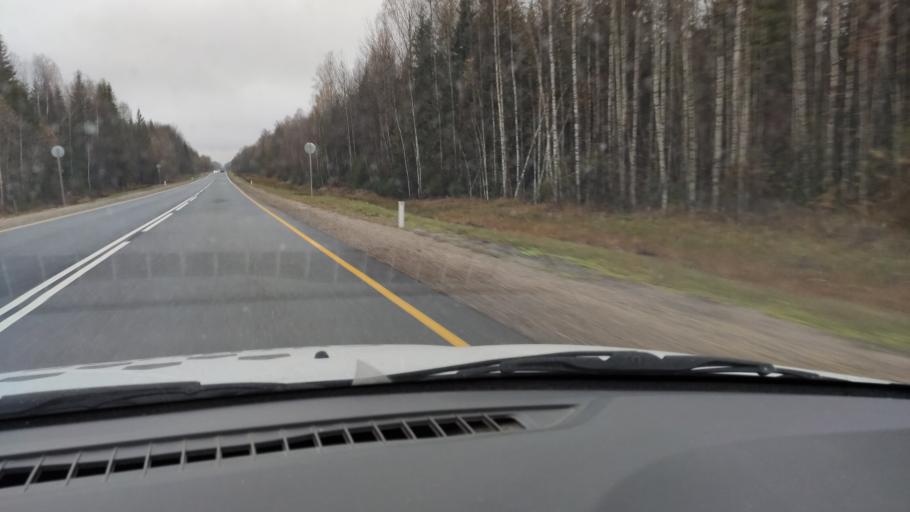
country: RU
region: Kirov
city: Chernaya Kholunitsa
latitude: 58.7774
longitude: 51.9232
